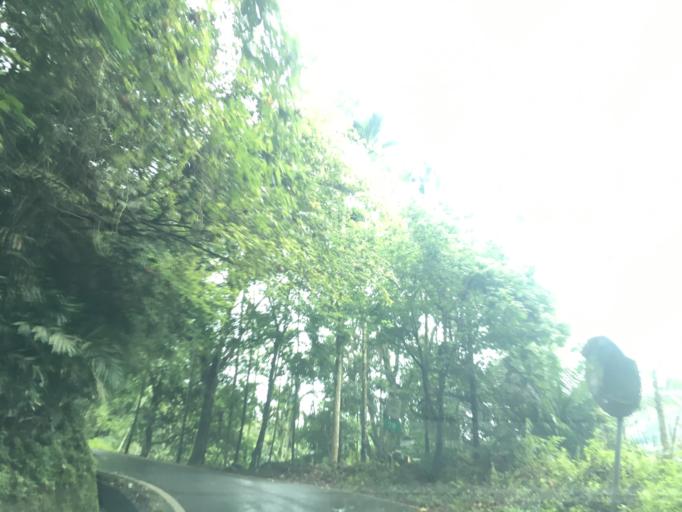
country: TW
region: Taiwan
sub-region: Yunlin
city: Douliu
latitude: 23.5637
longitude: 120.6484
